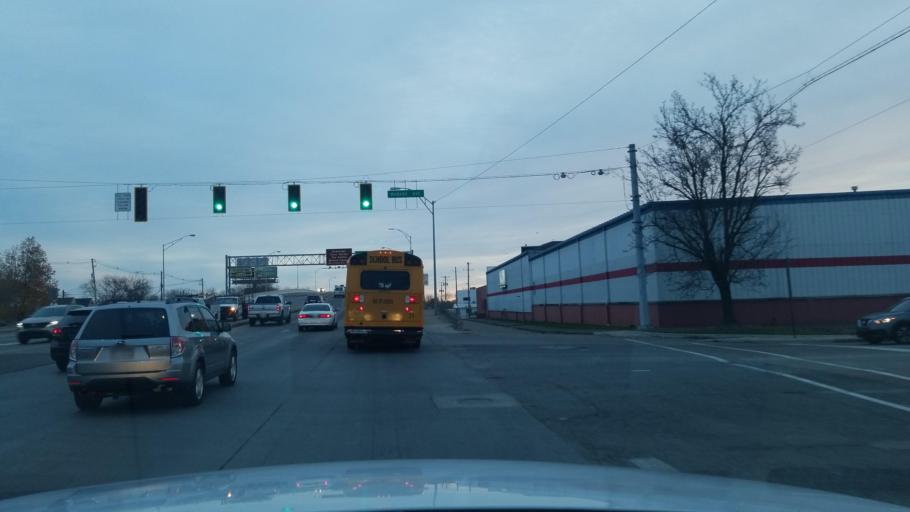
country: US
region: Indiana
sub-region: Vanderburgh County
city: Evansville
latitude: 37.9777
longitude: -87.5941
